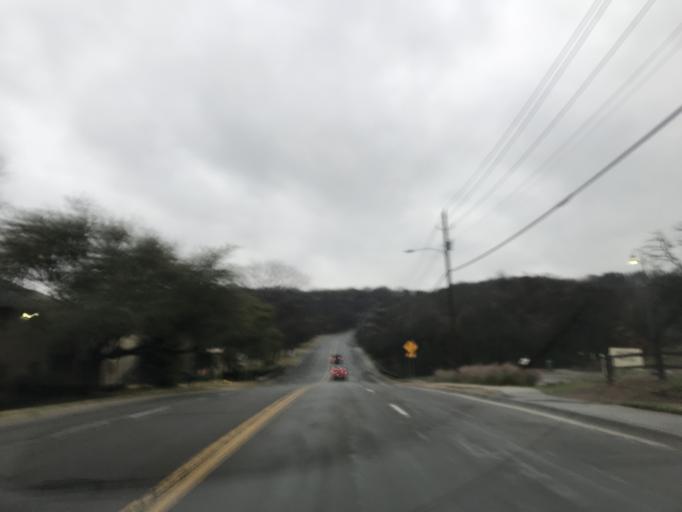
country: US
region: Texas
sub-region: Tarrant County
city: Arlington
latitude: 32.7753
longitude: -97.0946
